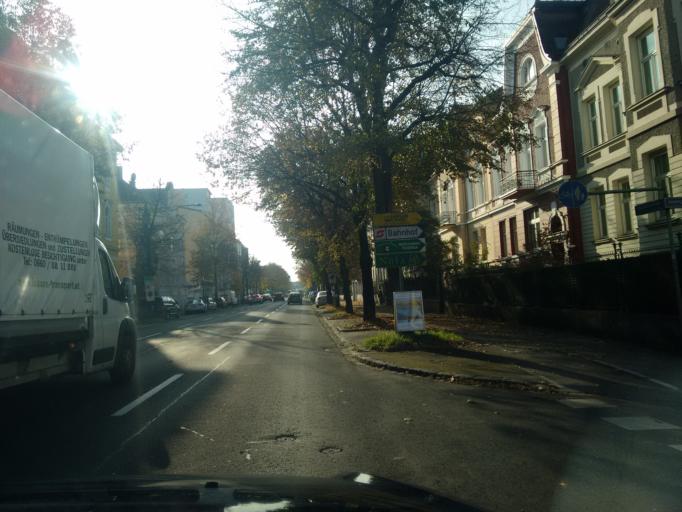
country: AT
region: Upper Austria
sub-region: Wels Stadt
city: Wels
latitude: 48.1626
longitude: 14.0240
